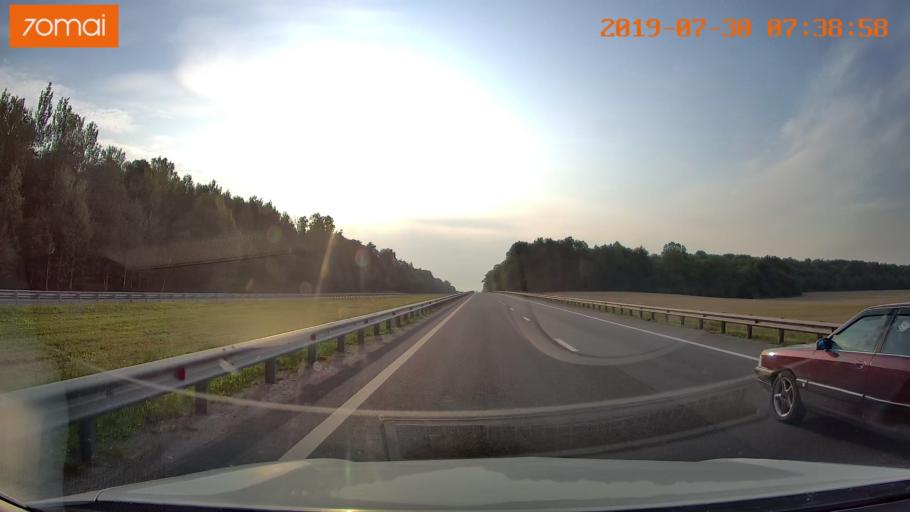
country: RU
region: Kaliningrad
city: Gvardeysk
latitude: 54.6494
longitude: 21.1829
